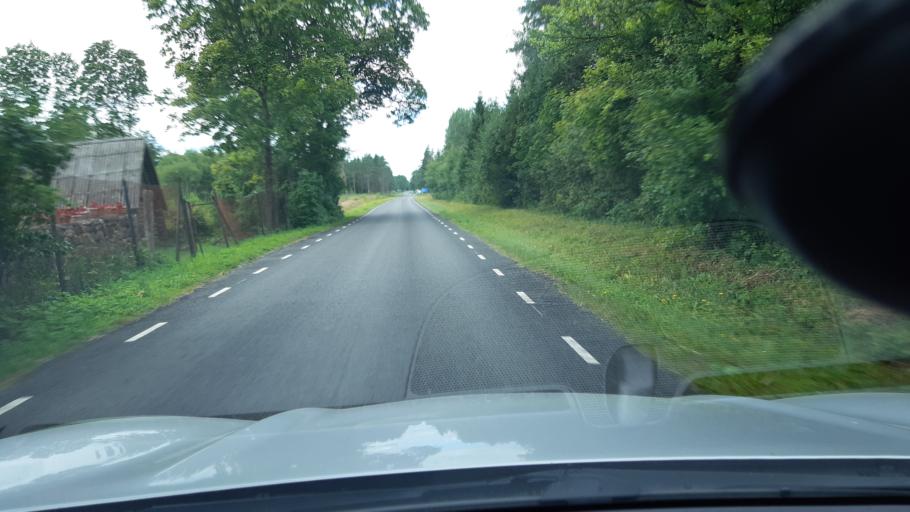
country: EE
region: Raplamaa
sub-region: Rapla vald
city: Rapla
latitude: 58.8844
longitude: 24.7301
